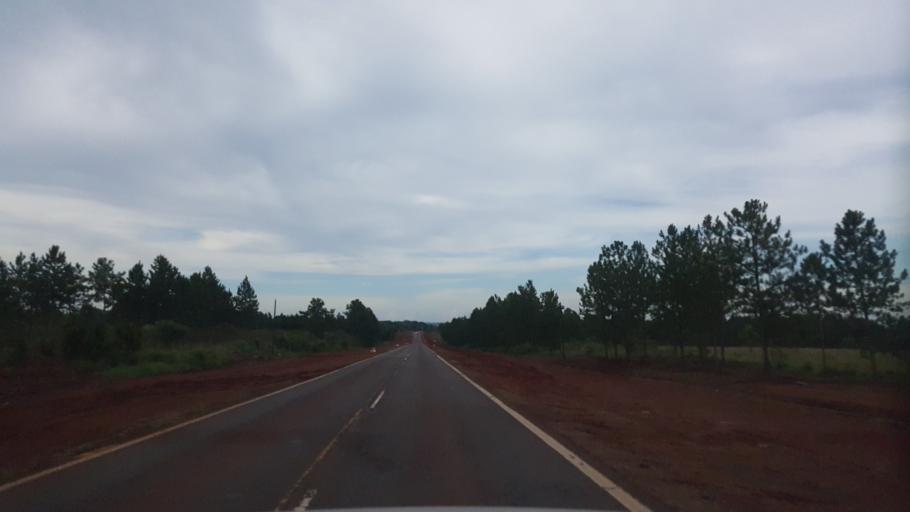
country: AR
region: Misiones
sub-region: Departamento de Candelaria
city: Loreto
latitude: -27.3468
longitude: -55.5472
